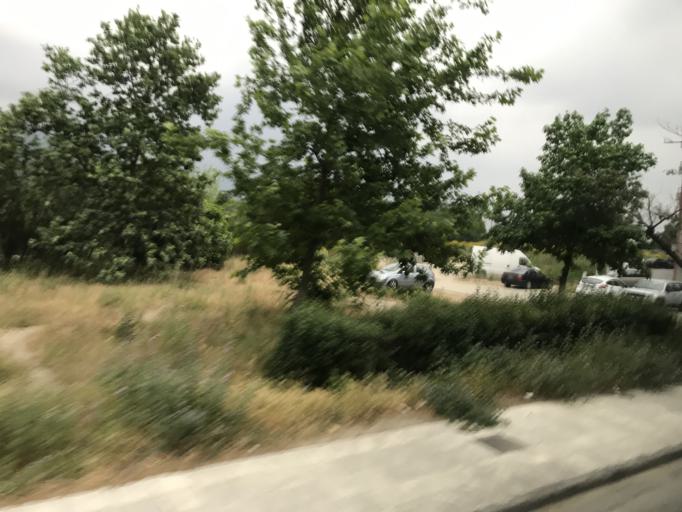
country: GR
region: East Macedonia and Thrace
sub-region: Nomos Xanthis
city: Xanthi
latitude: 41.1411
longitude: 24.8962
